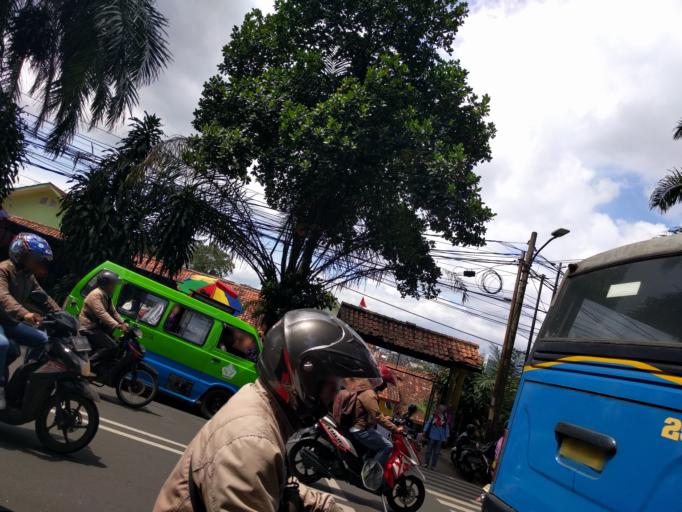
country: ID
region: West Java
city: Bogor
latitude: -6.6017
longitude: 106.8039
